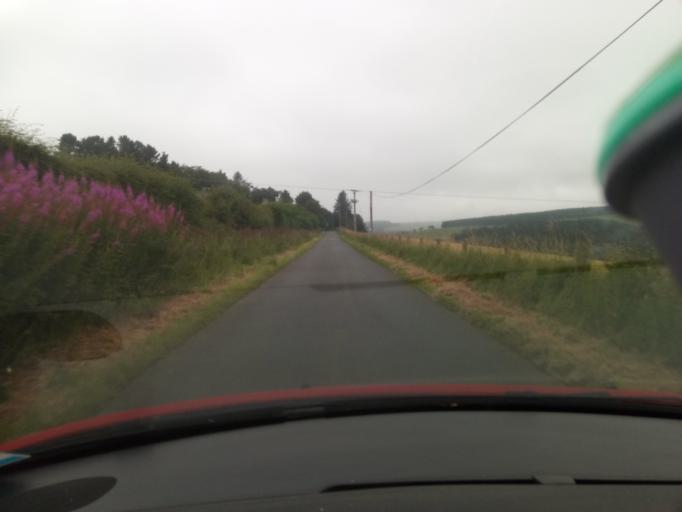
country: GB
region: Scotland
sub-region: The Scottish Borders
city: Galashiels
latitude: 55.7258
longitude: -2.8956
